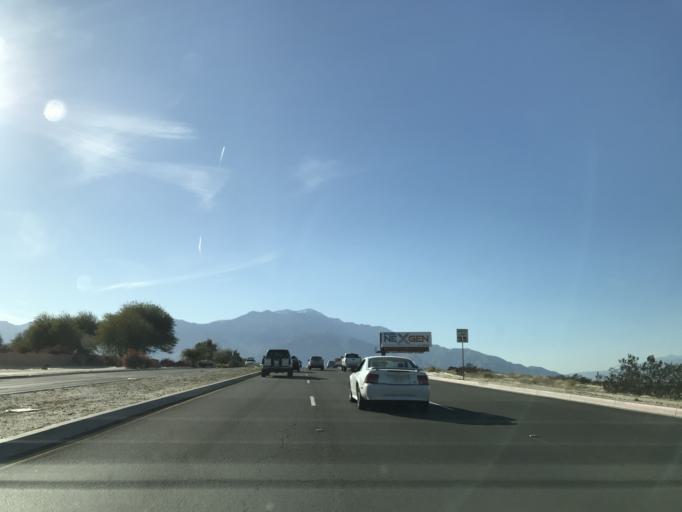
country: US
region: California
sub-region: Riverside County
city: Thousand Palms
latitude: 33.8163
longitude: -116.4247
